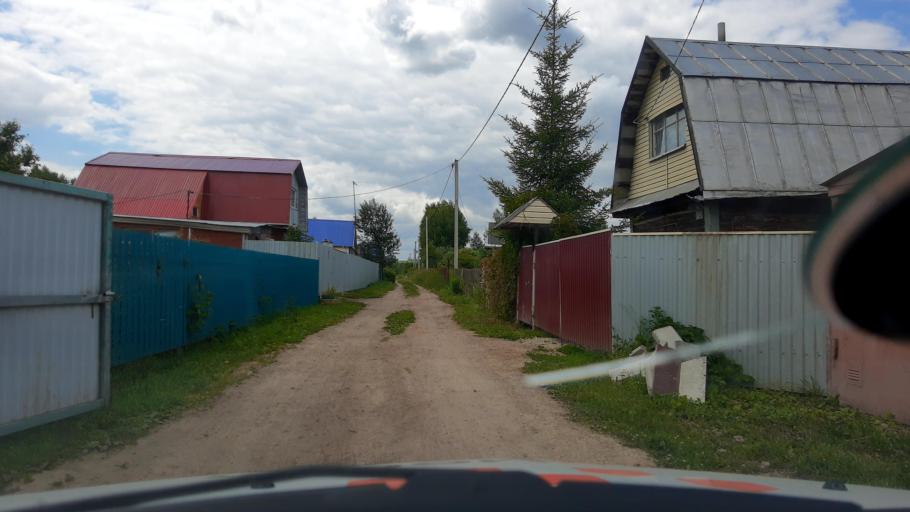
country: RU
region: Bashkortostan
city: Kabakovo
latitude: 54.7178
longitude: 56.2045
